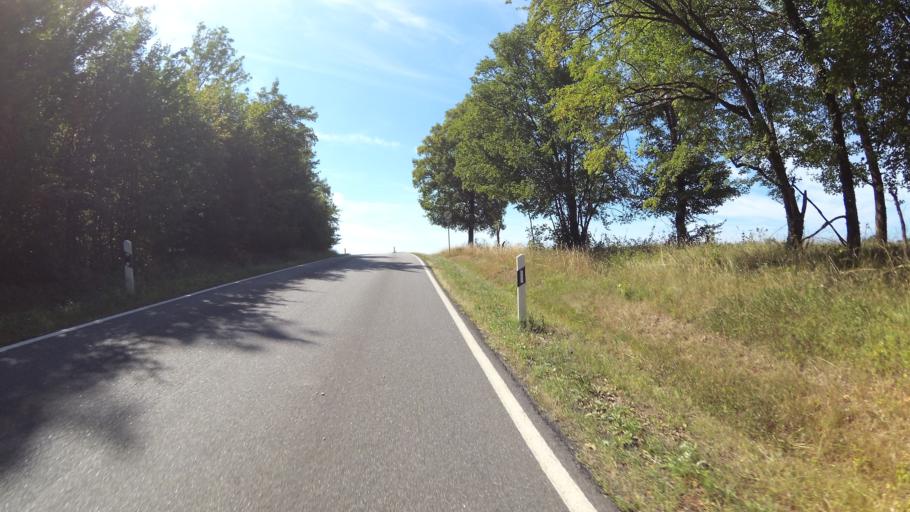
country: DE
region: Saarland
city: Gersheim
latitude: 49.1591
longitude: 7.2648
